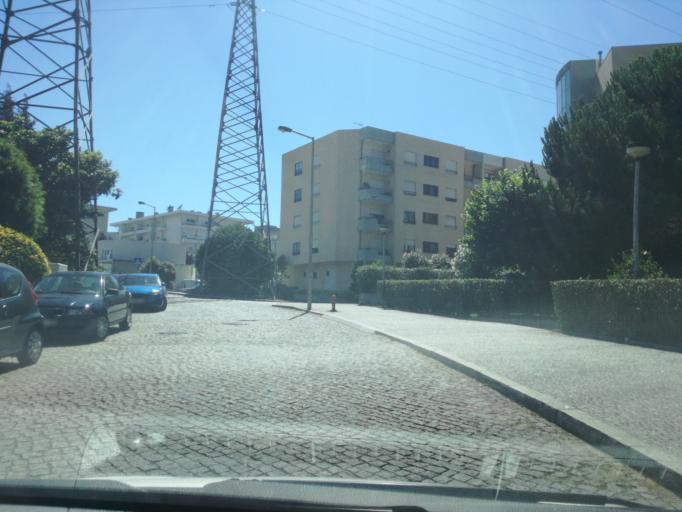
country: PT
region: Porto
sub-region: Maia
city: Maia
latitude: 41.2382
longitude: -8.6116
